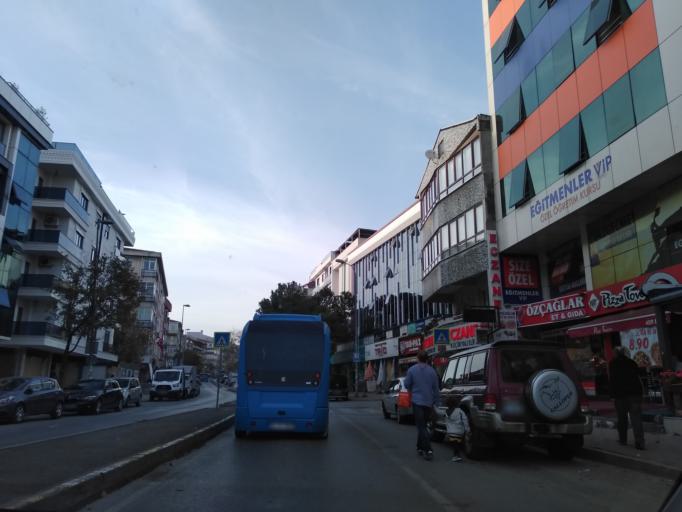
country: TR
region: Istanbul
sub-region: Atasehir
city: Atasehir
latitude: 40.9501
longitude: 29.1045
